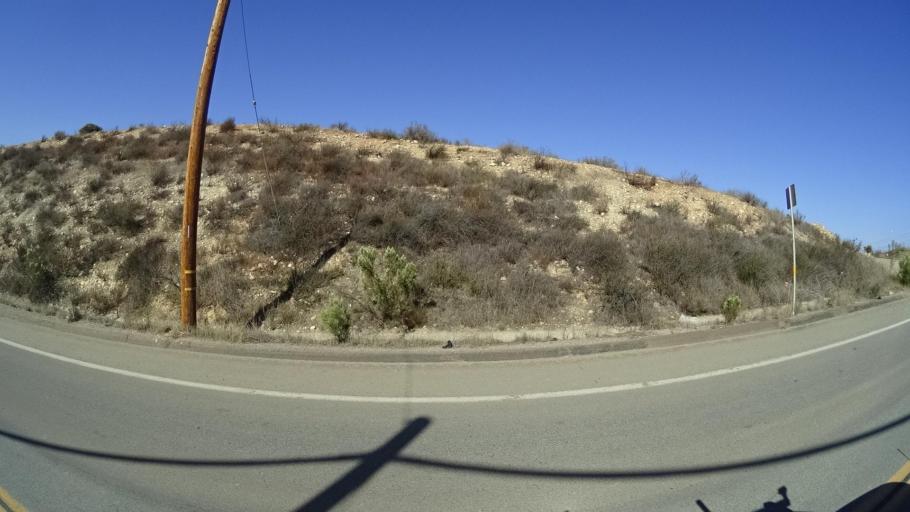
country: MX
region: Baja California
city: Tijuana
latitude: 32.5903
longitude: -116.9273
